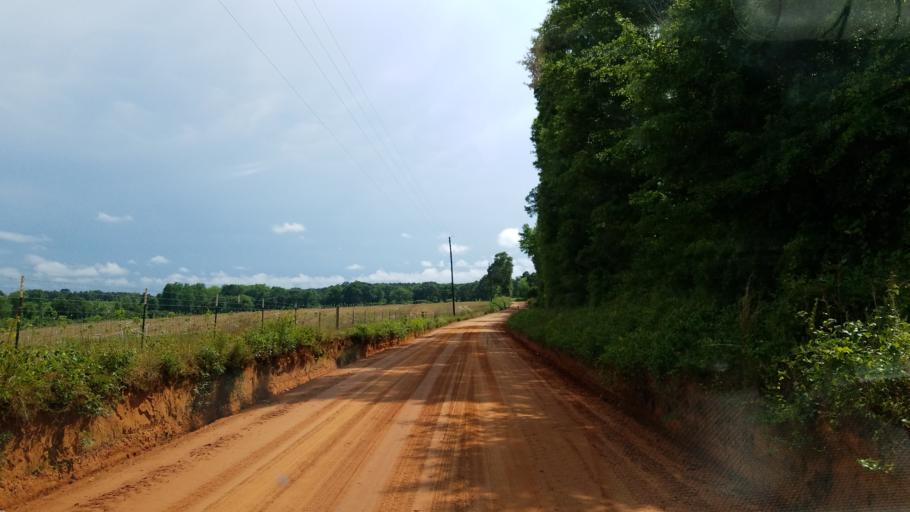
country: US
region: Georgia
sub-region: Houston County
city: Perry
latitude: 32.4505
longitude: -83.7851
